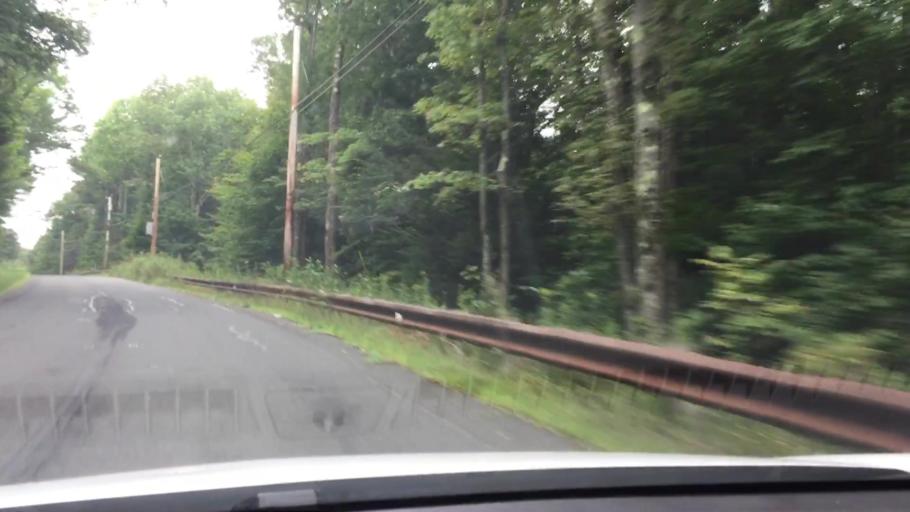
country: US
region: Massachusetts
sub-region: Berkshire County
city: Becket
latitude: 42.2615
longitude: -73.0009
